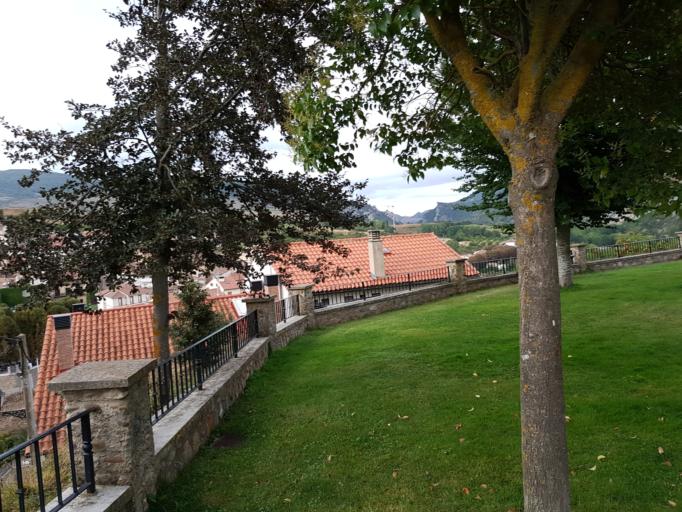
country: ES
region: La Rioja
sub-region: Provincia de La Rioja
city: Torrecilla en Cameros
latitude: 42.2547
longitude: -2.6320
